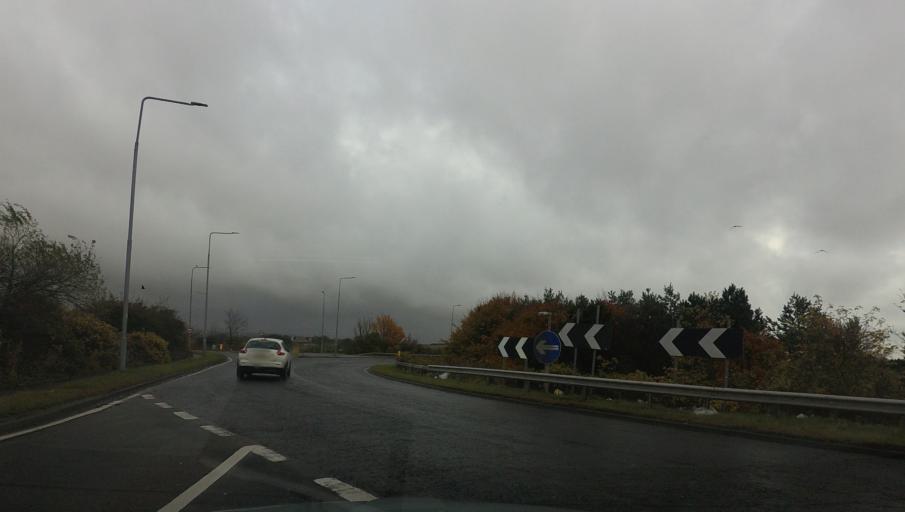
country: GB
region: Scotland
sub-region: Fife
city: Cardenden
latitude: 56.1384
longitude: -3.2109
